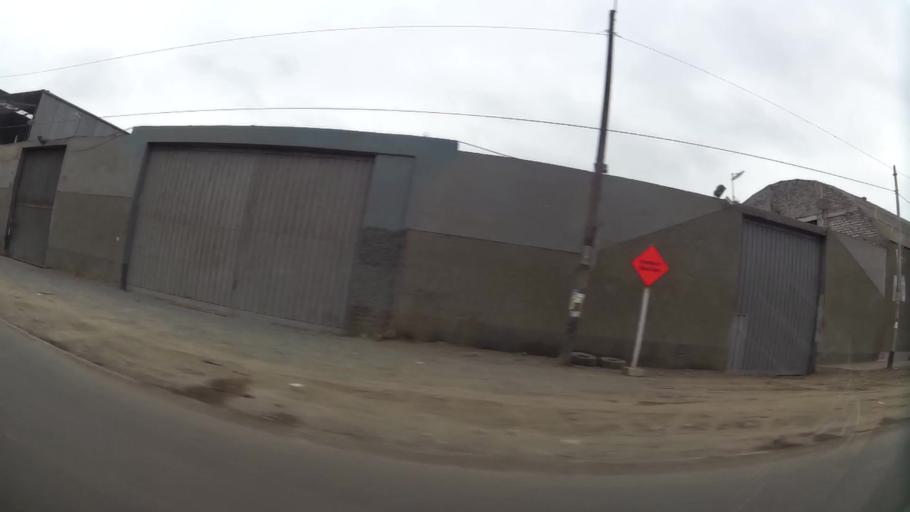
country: PE
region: Lima
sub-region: Lima
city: Vitarte
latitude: -12.0487
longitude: -76.9574
